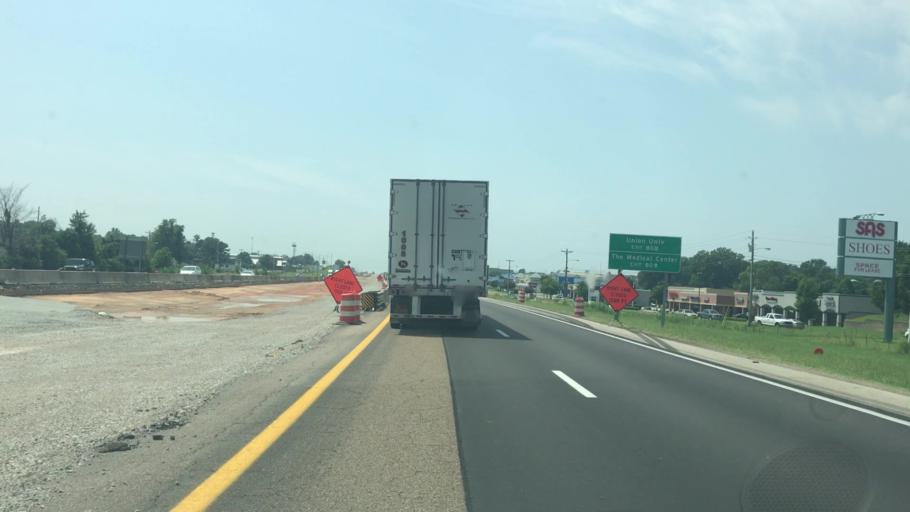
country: US
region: Tennessee
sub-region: Madison County
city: Jackson
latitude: 35.6697
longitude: -88.8359
